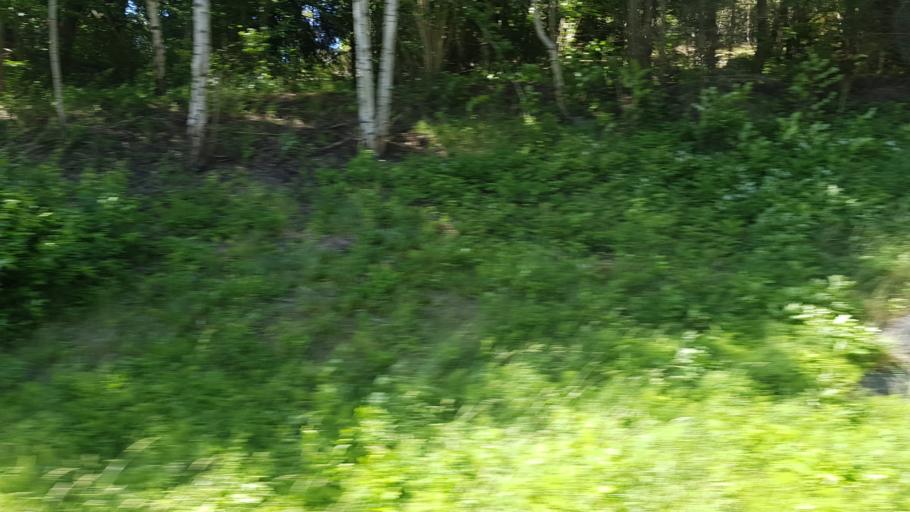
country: SE
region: Vaestra Goetaland
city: Ronnang
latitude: 57.9936
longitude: 11.6612
